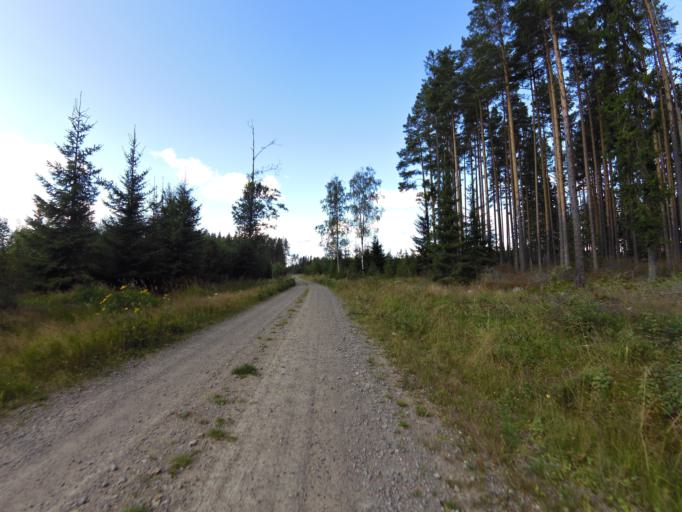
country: SE
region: Gaevleborg
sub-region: Ockelbo Kommun
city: Ockelbo
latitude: 60.8113
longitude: 16.7702
